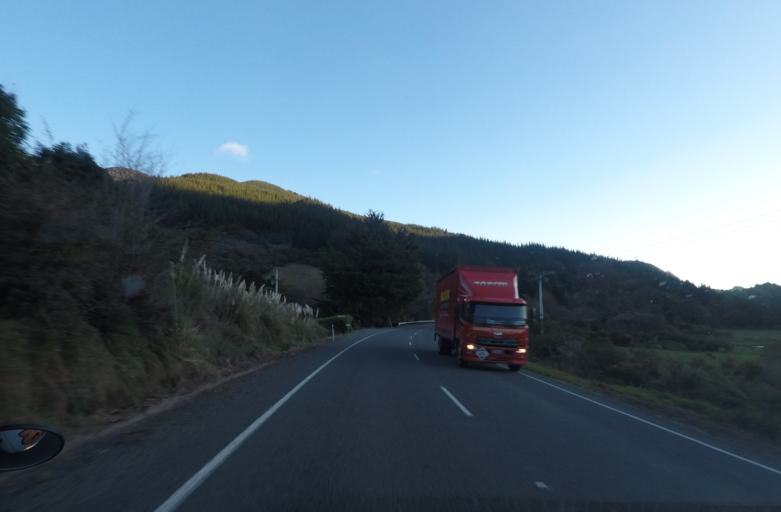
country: NZ
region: Marlborough
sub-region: Marlborough District
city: Picton
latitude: -41.2821
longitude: 173.7266
